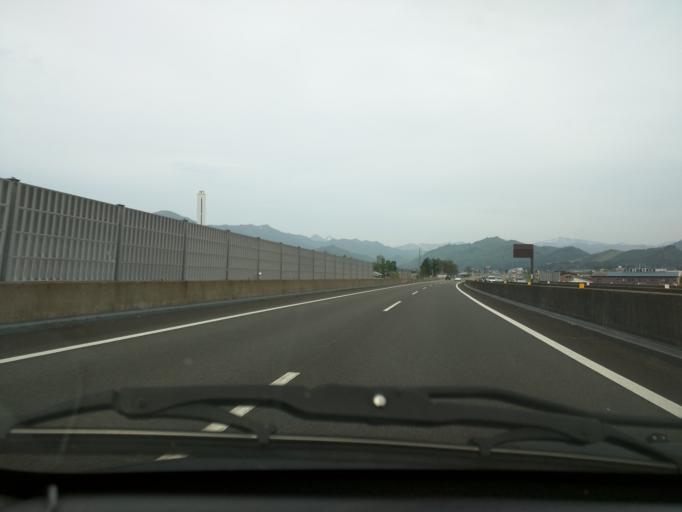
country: JP
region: Niigata
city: Ojiya
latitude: 37.2437
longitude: 138.9570
